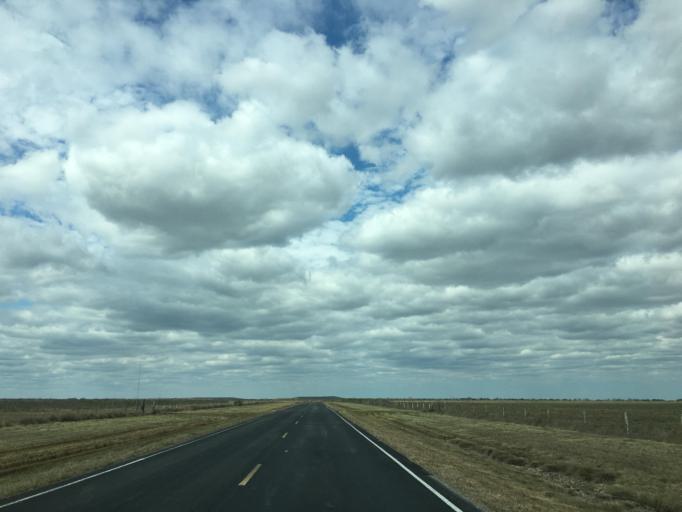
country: US
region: Texas
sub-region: Brazoria County
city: Oyster Creek
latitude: 29.0644
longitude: -95.2918
